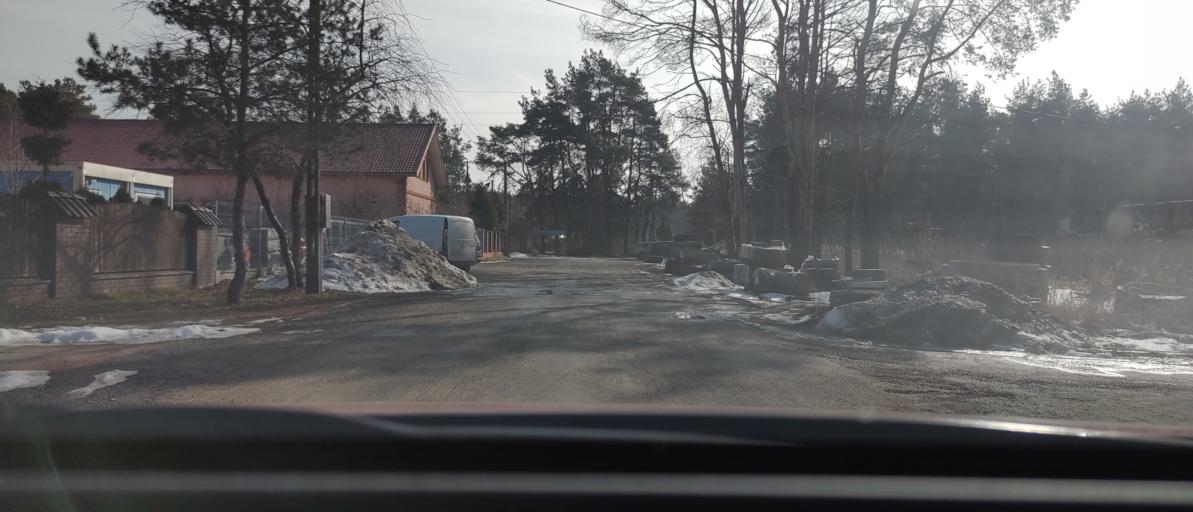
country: PL
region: Masovian Voivodeship
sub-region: Powiat bialobrzeski
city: Bialobrzegi
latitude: 51.6457
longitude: 20.9392
